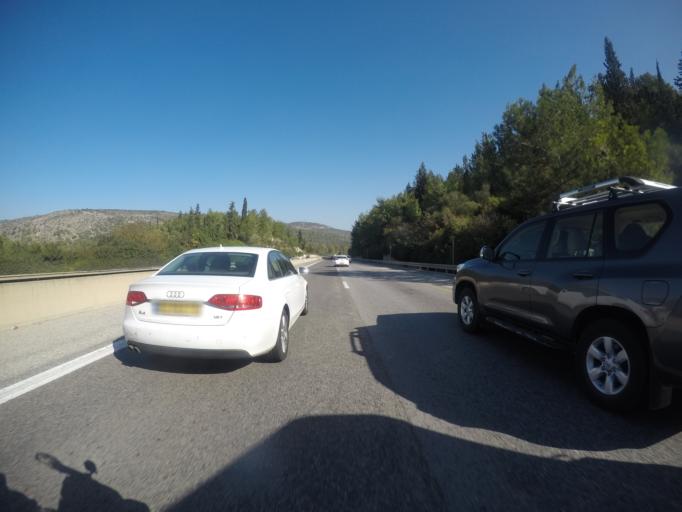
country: IL
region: Haifa
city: Daliyat el Karmil
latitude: 32.6457
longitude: 35.0809
